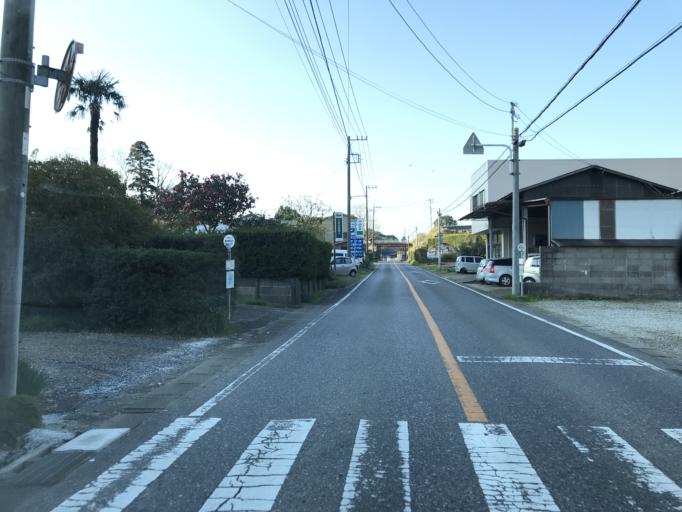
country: JP
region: Chiba
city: Yokaichiba
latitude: 35.7354
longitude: 140.5568
